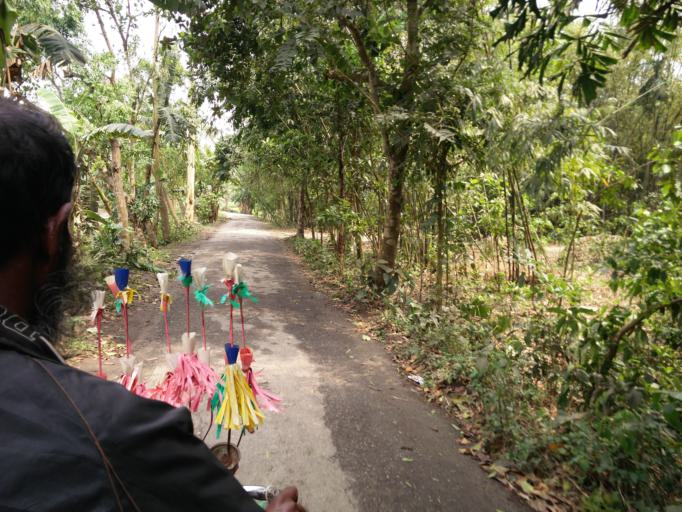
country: BD
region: Dhaka
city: Sherpur
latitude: 24.9335
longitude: 90.1617
